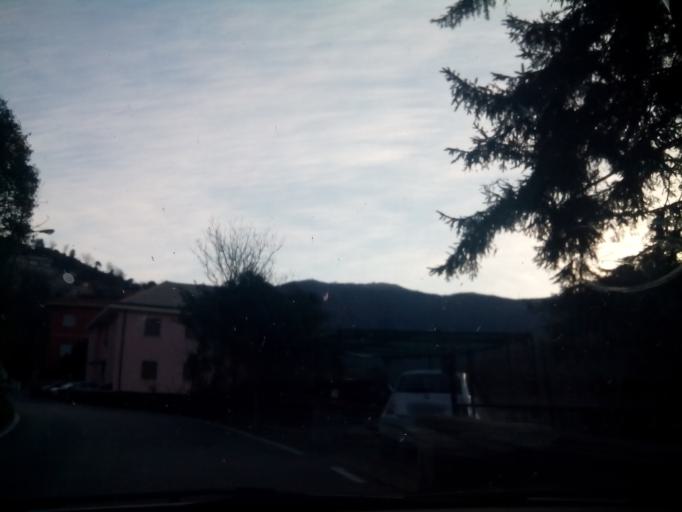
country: IT
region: Liguria
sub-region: Provincia di Genova
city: Piccarello
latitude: 44.4184
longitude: 9.0014
